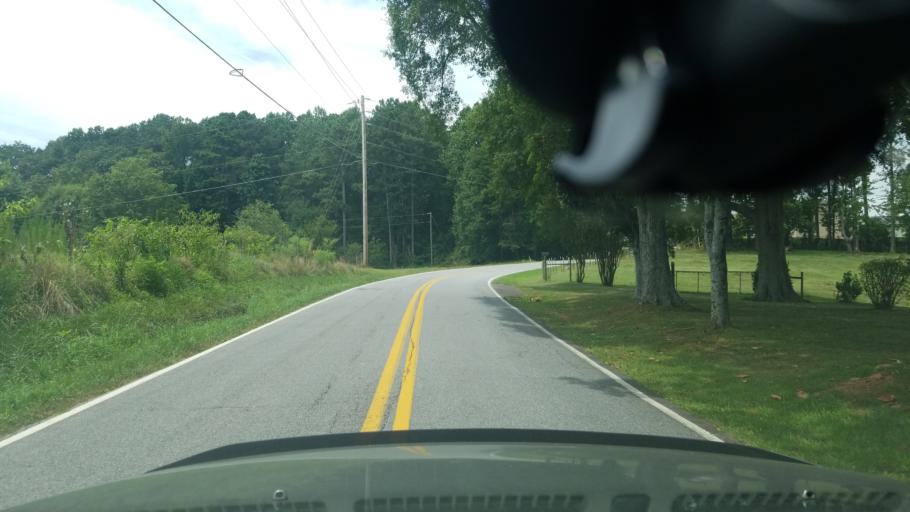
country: US
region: Georgia
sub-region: Forsyth County
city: Cumming
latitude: 34.2250
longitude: -84.2126
